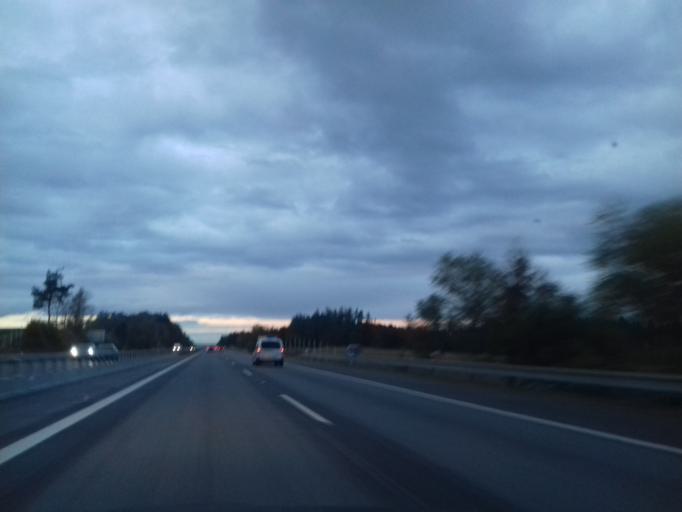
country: CZ
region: Central Bohemia
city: Cechtice
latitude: 49.6365
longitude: 15.1277
